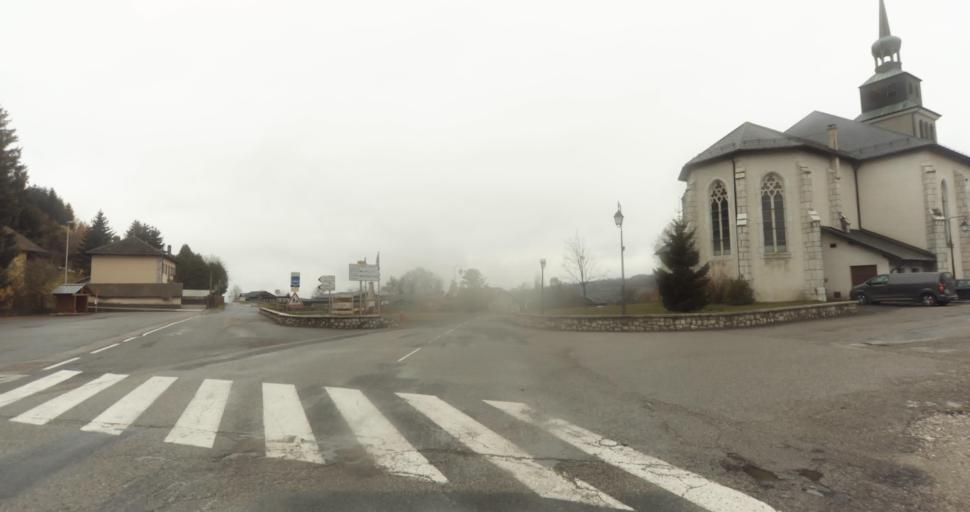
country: FR
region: Rhone-Alpes
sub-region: Departement de la Haute-Savoie
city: Evires
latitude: 46.0373
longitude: 6.2250
